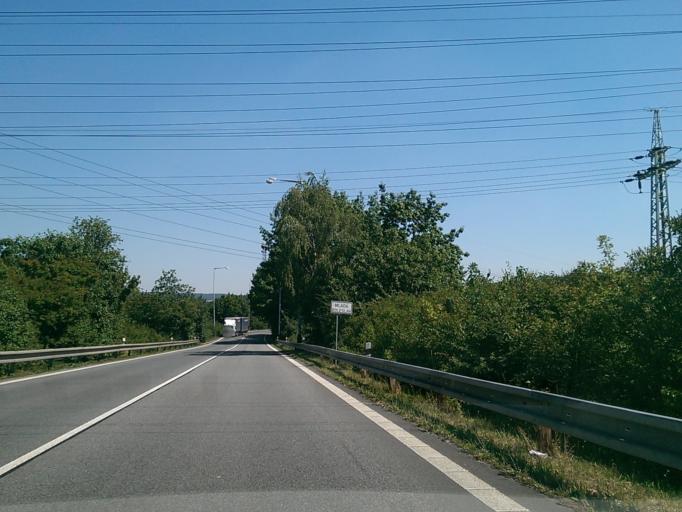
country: CZ
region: Central Bohemia
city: Kosmonosy
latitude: 50.4112
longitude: 14.9399
